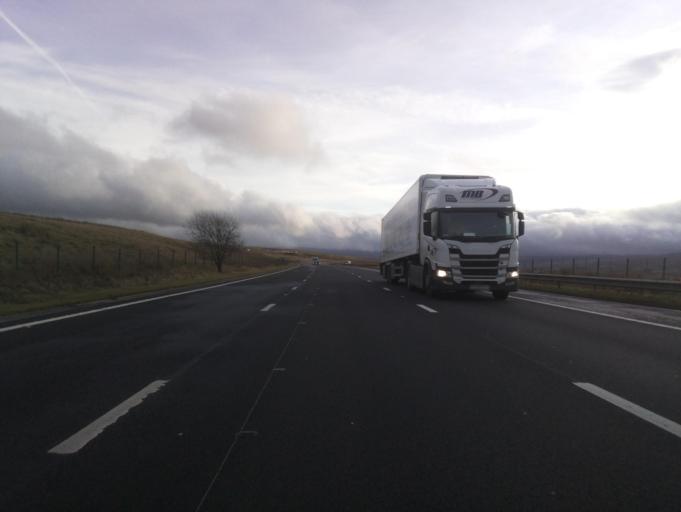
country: GB
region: England
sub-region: Cumbria
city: Appleby-in-Westmorland
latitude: 54.4887
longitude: -2.6403
